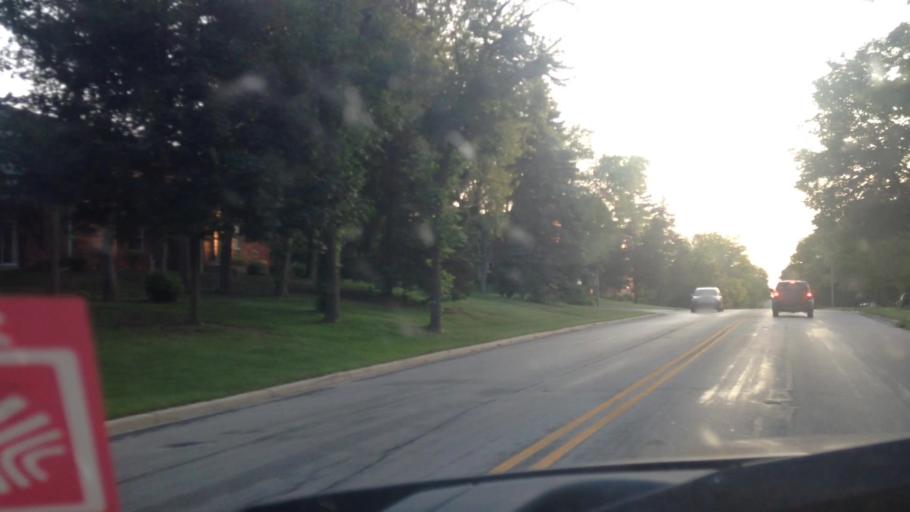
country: US
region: Wisconsin
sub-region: Waukesha County
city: Menomonee Falls
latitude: 43.1703
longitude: -88.1073
